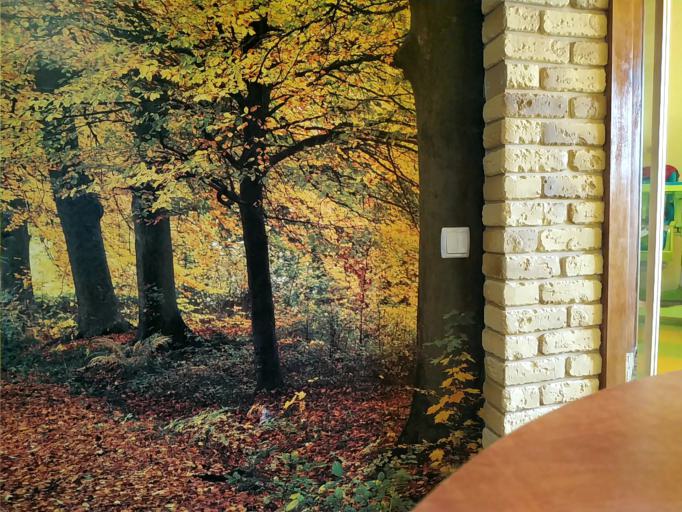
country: RU
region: Vologda
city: Nelazskoye
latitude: 59.4151
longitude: 37.6084
